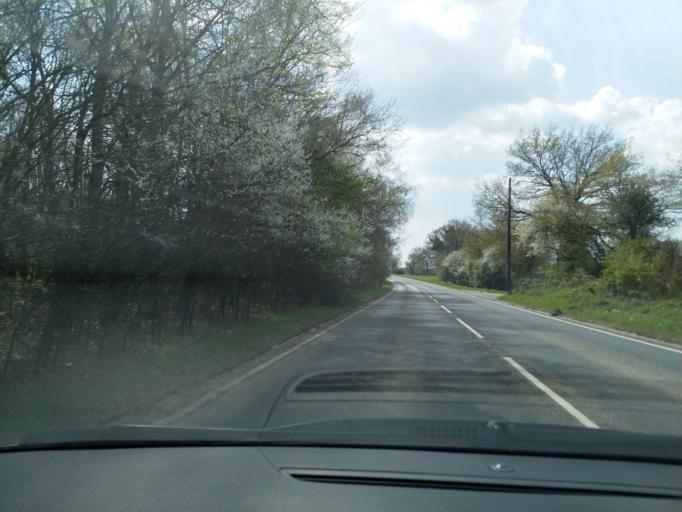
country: GB
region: England
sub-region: Warwickshire
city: Ryton on Dunsmore
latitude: 52.3393
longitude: -1.4820
